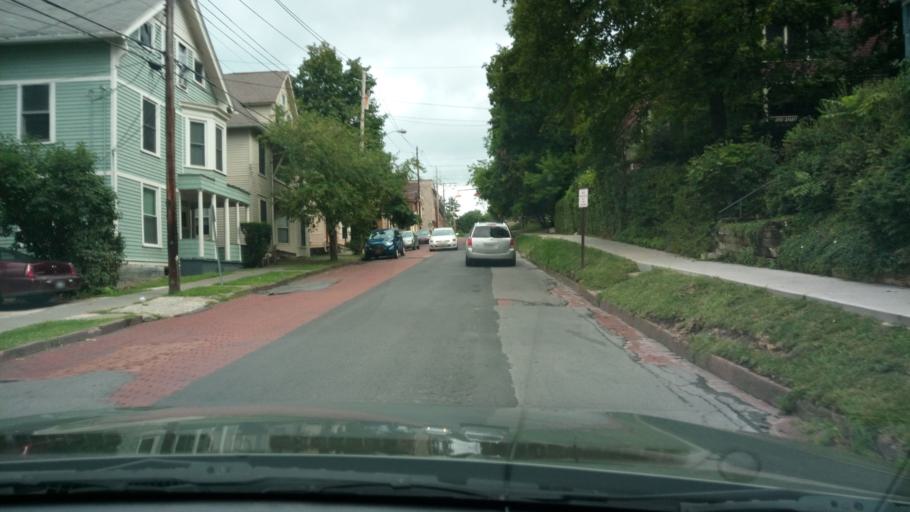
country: US
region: New York
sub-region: Tompkins County
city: Ithaca
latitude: 42.4407
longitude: -76.4898
